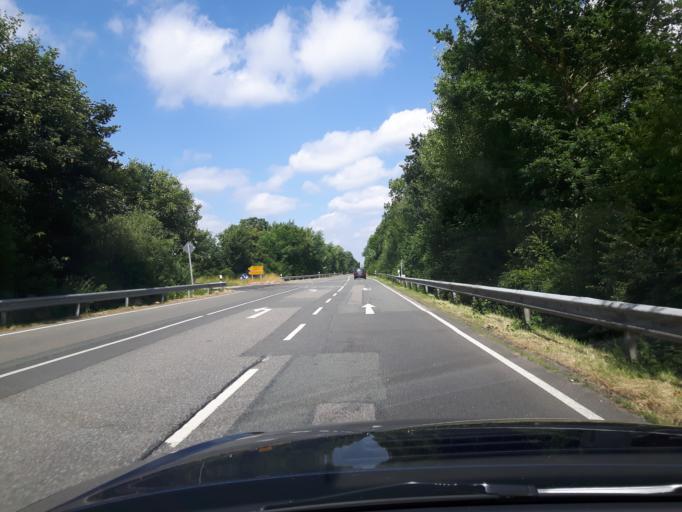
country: DE
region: Schleswig-Holstein
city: Sierksdorf
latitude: 54.0628
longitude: 10.7559
